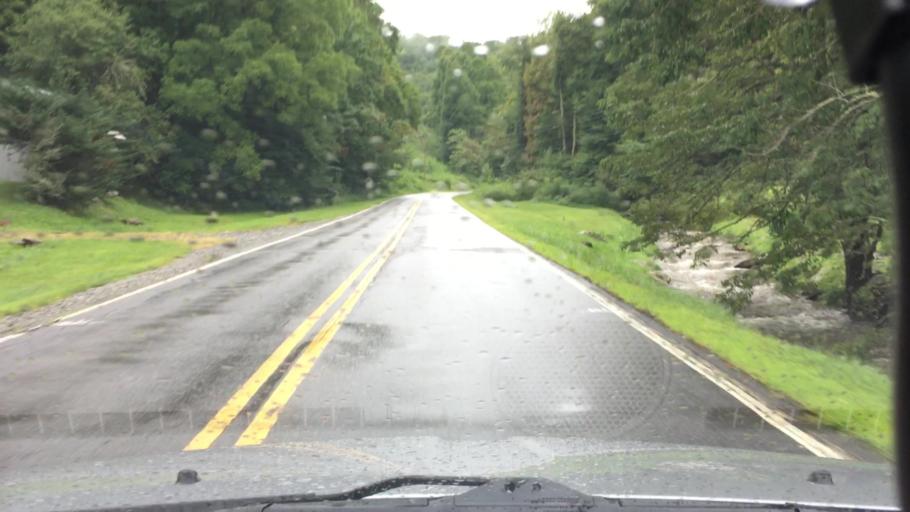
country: US
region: North Carolina
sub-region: Madison County
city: Mars Hill
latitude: 35.9190
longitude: -82.5389
